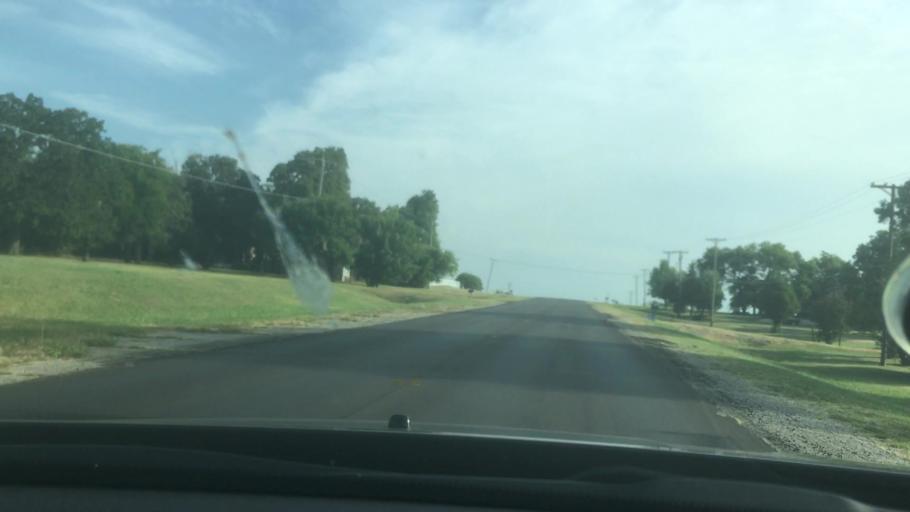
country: US
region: Oklahoma
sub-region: Pontotoc County
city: Ada
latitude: 34.7458
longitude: -96.6701
